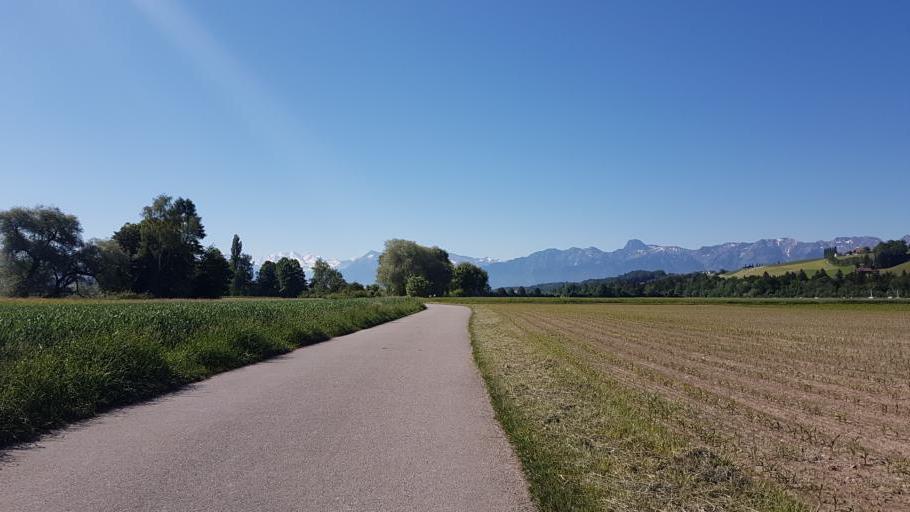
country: CH
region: Bern
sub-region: Bern-Mittelland District
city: Munsingen
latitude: 46.8640
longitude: 7.5582
